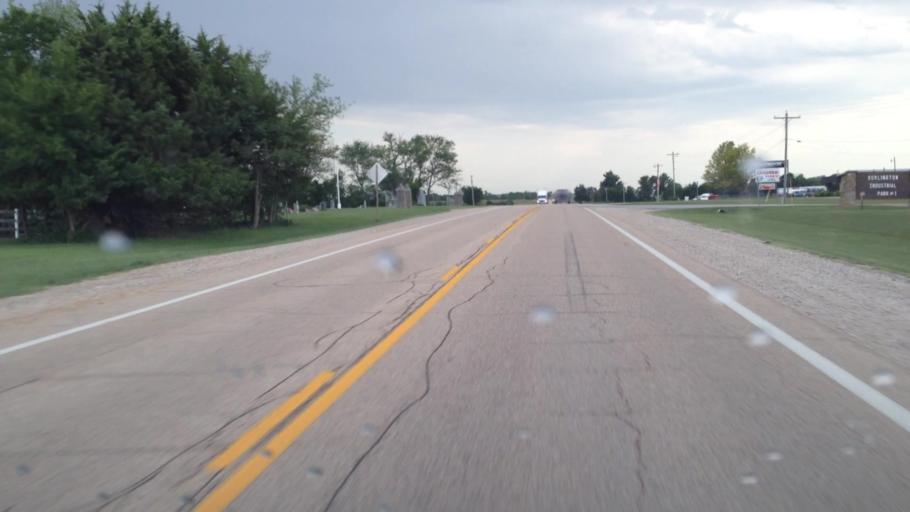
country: US
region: Kansas
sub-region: Coffey County
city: Burlington
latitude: 38.1792
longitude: -95.7388
